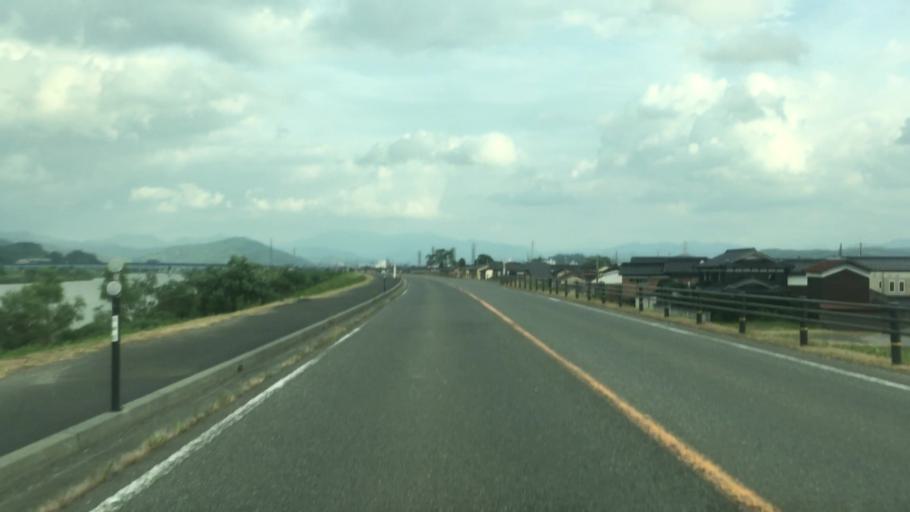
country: JP
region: Hyogo
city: Toyooka
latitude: 35.5636
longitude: 134.8125
